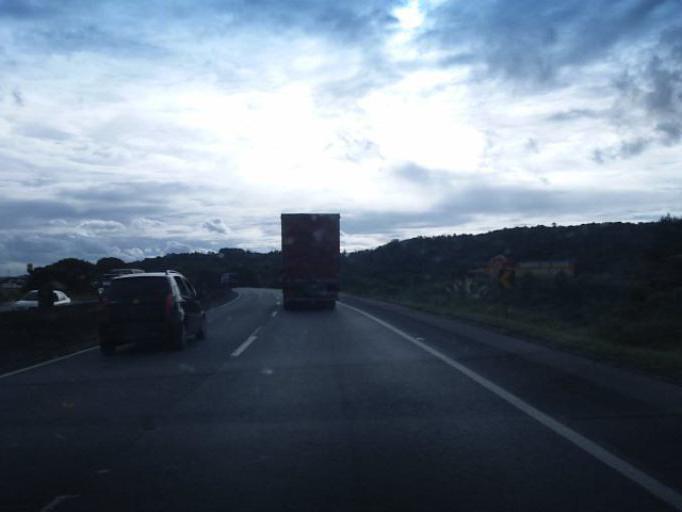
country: BR
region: Parana
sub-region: Campina Grande Do Sul
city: Campina Grande do Sul
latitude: -25.3109
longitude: -49.0143
